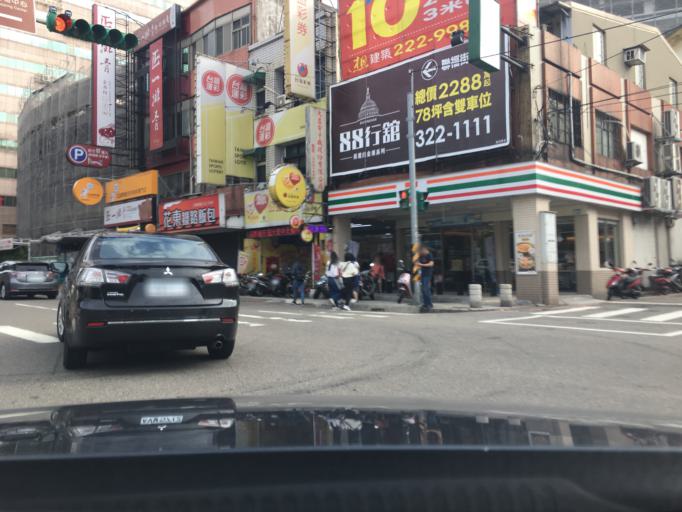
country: TW
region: Taiwan
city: Taoyuan City
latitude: 25.0521
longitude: 121.2874
